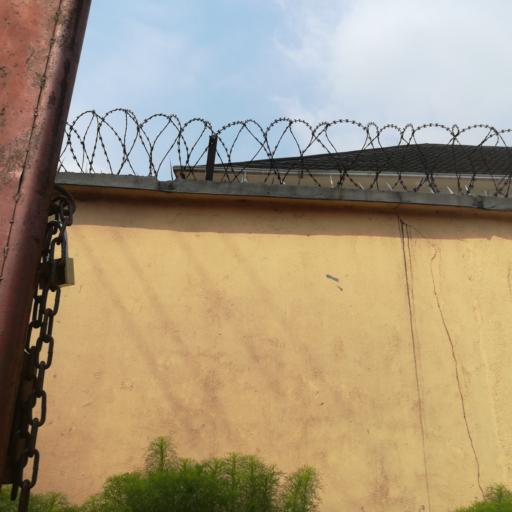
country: NG
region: Rivers
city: Port Harcourt
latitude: 4.8352
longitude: 7.0651
